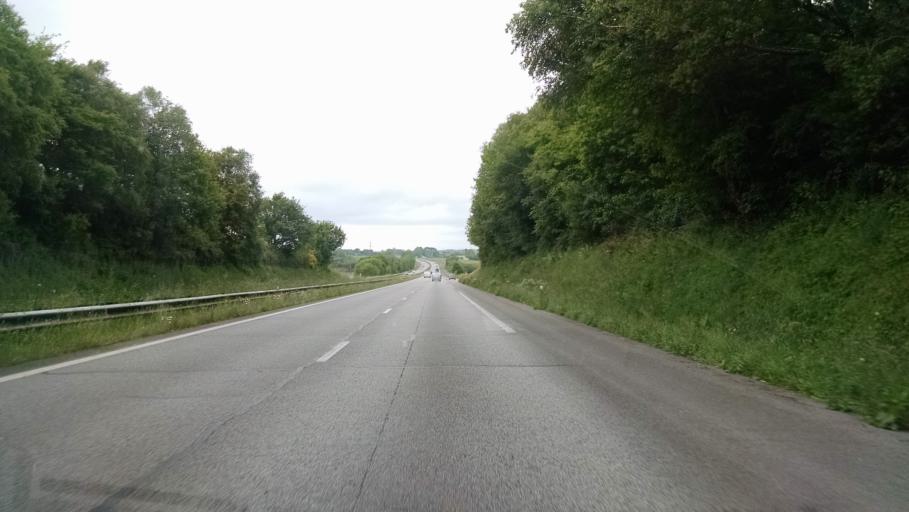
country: FR
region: Brittany
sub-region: Departement du Finistere
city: Landrevarzec
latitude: 48.0596
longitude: -4.0527
